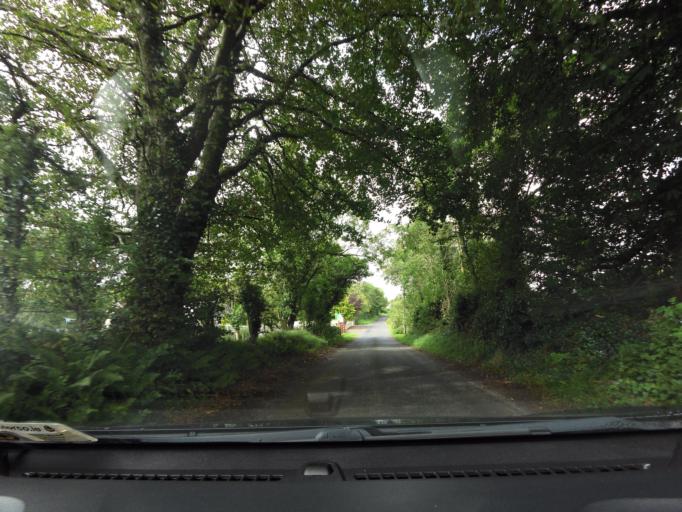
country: IE
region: Connaught
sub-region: County Galway
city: Loughrea
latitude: 53.3018
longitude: -8.6023
